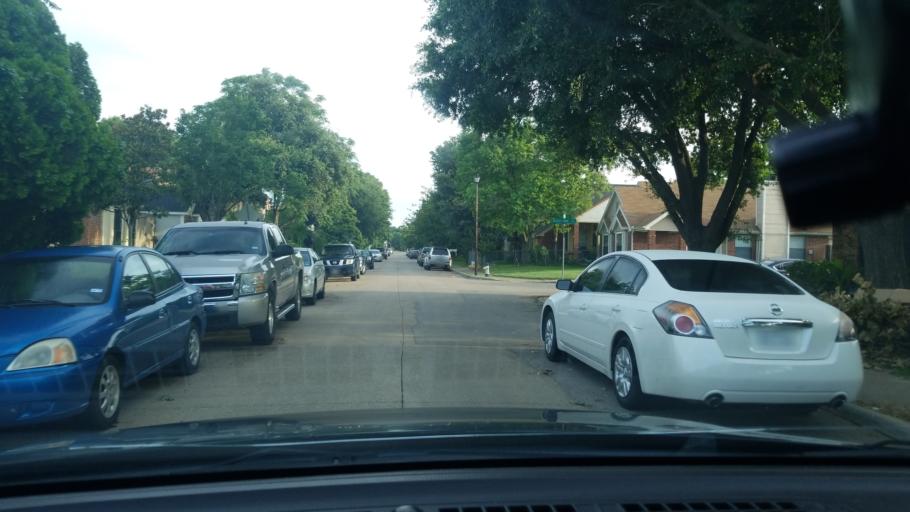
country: US
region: Texas
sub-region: Dallas County
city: Balch Springs
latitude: 32.7546
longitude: -96.6432
